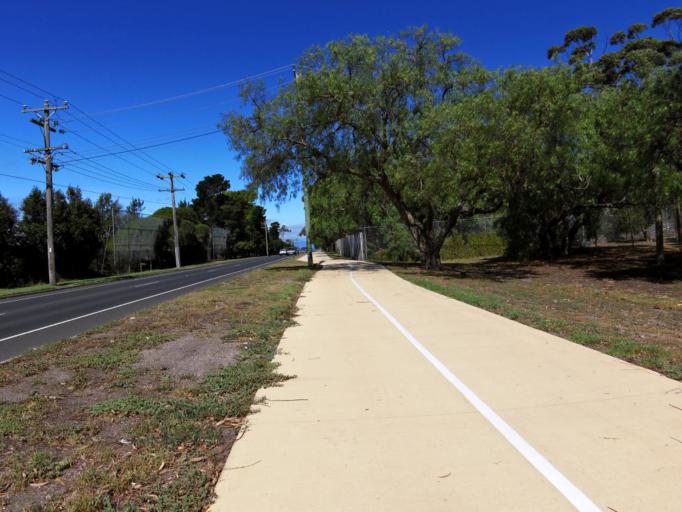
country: AU
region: Victoria
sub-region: Hobsons Bay
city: Altona Meadows
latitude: -37.8765
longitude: 144.8038
